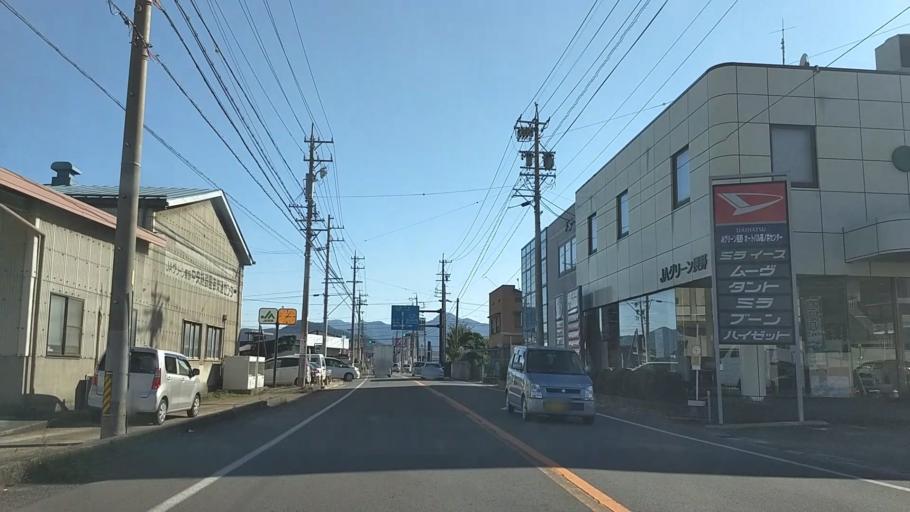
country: JP
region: Nagano
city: Nagano-shi
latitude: 36.5706
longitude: 138.1419
